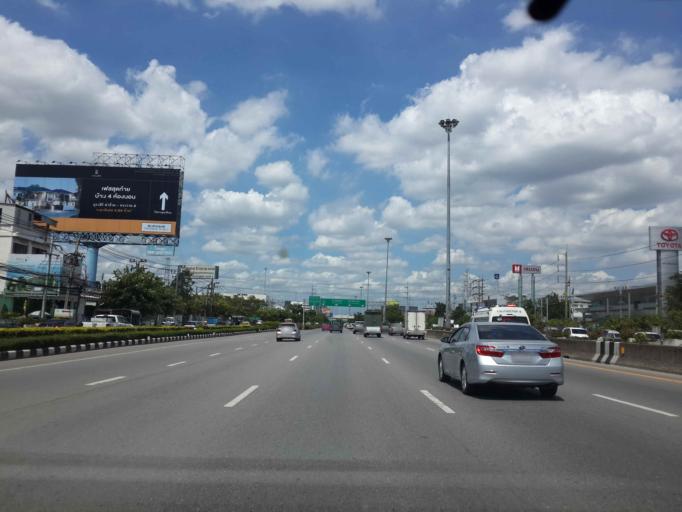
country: TH
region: Bangkok
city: Bang Khun Thian
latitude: 13.6509
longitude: 100.4218
